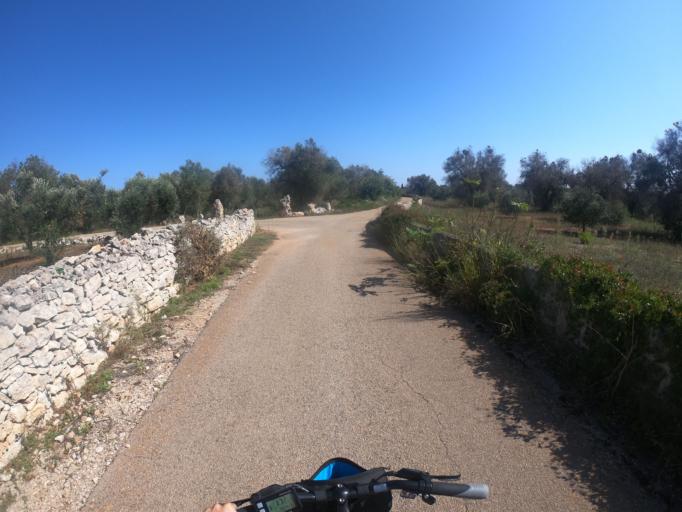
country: IT
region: Apulia
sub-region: Provincia di Lecce
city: Specchia
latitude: 39.9208
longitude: 18.2840
